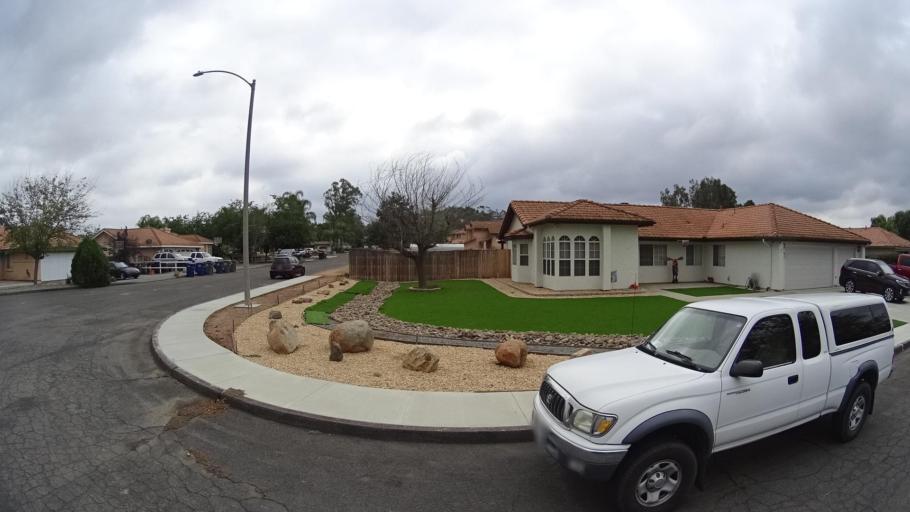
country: US
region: California
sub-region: San Diego County
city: Ramona
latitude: 33.0271
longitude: -116.8760
